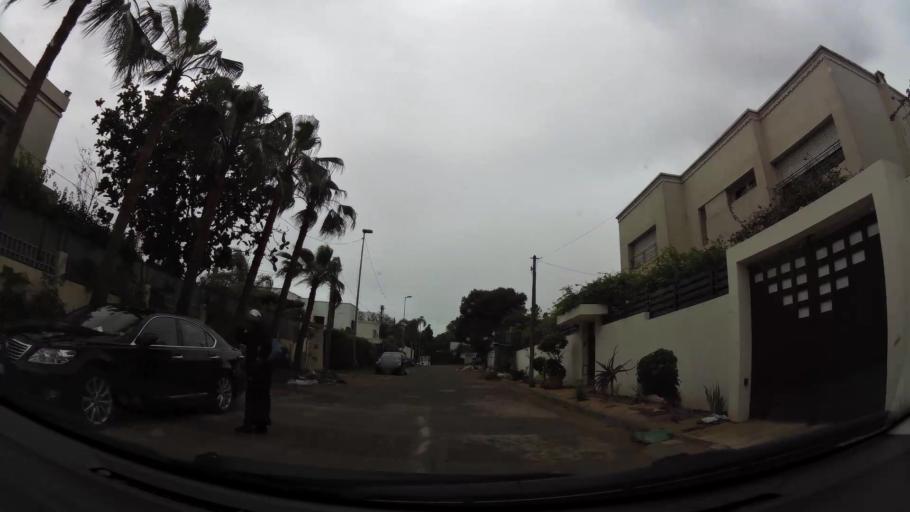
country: MA
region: Grand Casablanca
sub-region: Casablanca
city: Casablanca
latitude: 33.5941
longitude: -7.6593
